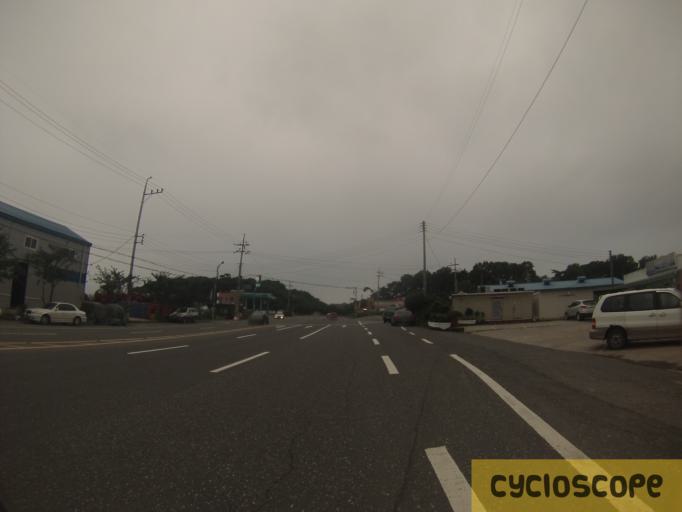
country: KR
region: Chungcheongnam-do
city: Taisen-ri
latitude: 36.3873
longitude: 126.6526
